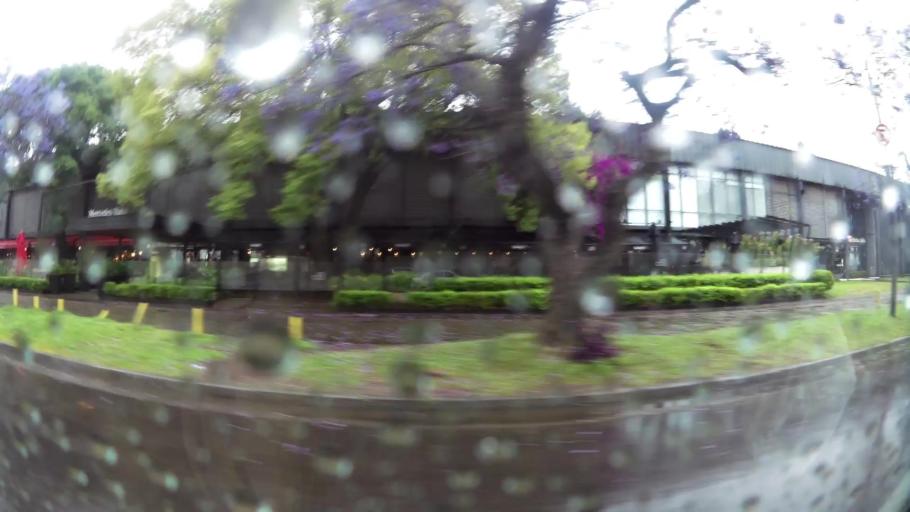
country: AR
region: Buenos Aires F.D.
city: Retiro
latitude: -34.5834
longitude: -58.3925
